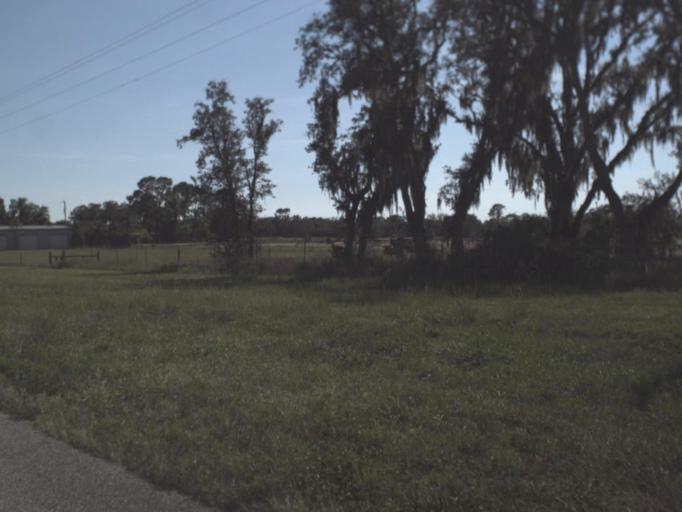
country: US
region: Florida
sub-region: Highlands County
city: Lake Placid
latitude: 27.3876
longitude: -81.4118
